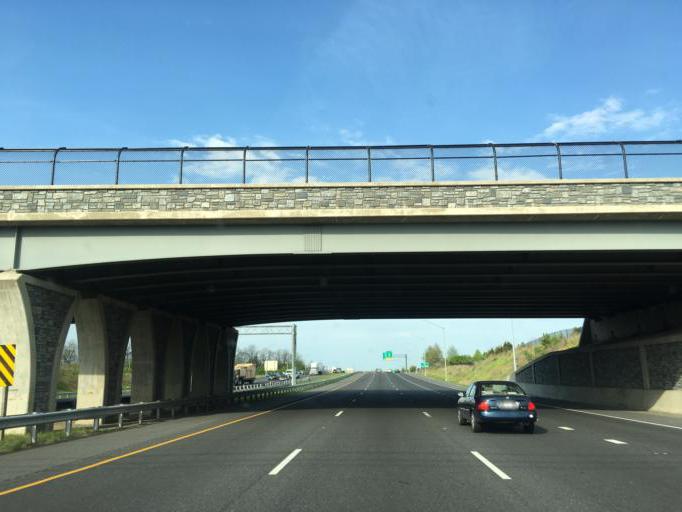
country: US
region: Maryland
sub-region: Frederick County
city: Frederick
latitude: 39.4002
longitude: -77.4090
